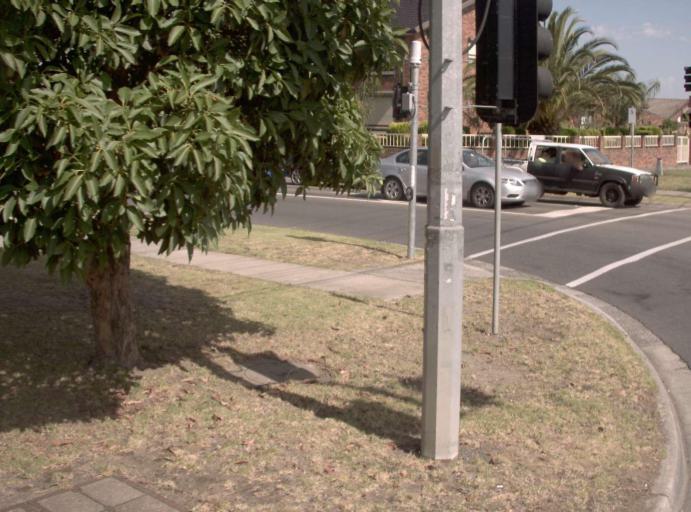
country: AU
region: Victoria
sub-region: Monash
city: Mulgrave
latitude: -37.9131
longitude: 145.1880
